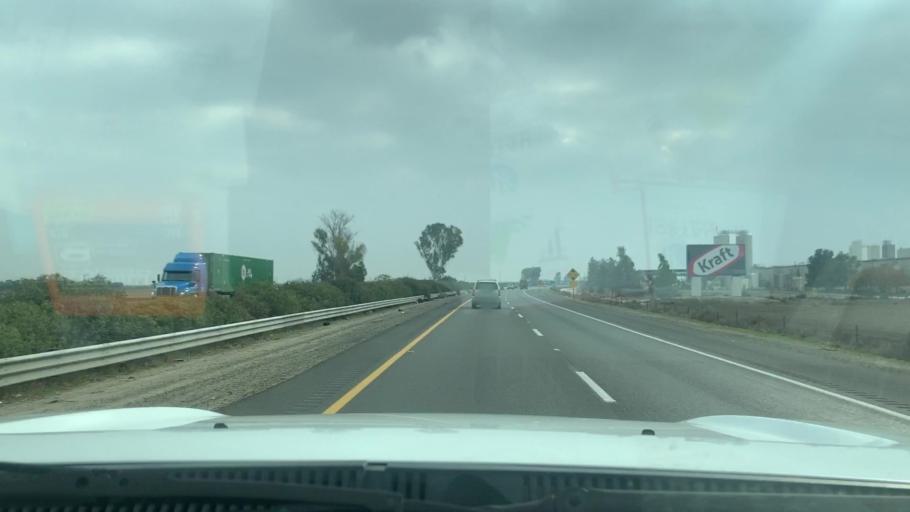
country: US
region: California
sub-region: Tulare County
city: Tulare
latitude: 36.1346
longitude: -119.3262
